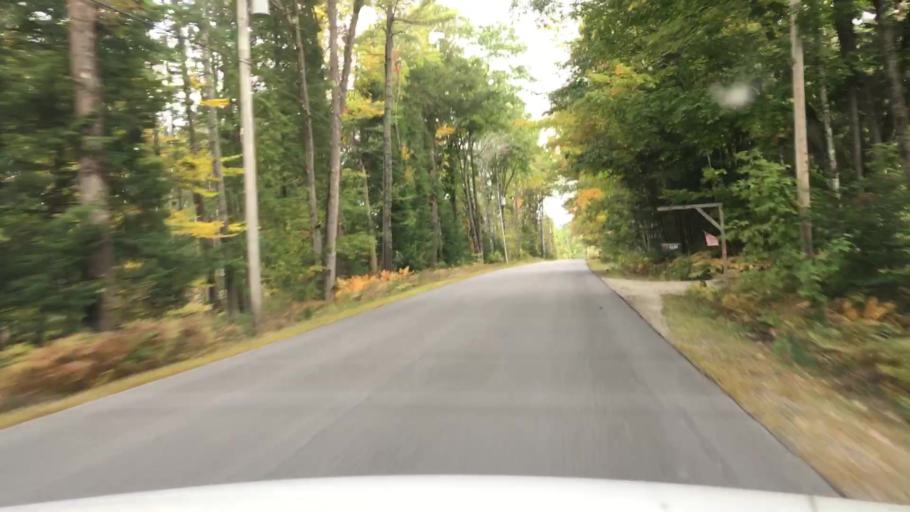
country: US
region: Maine
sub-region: Cumberland County
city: Harrison
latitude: 44.2481
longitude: -70.7211
